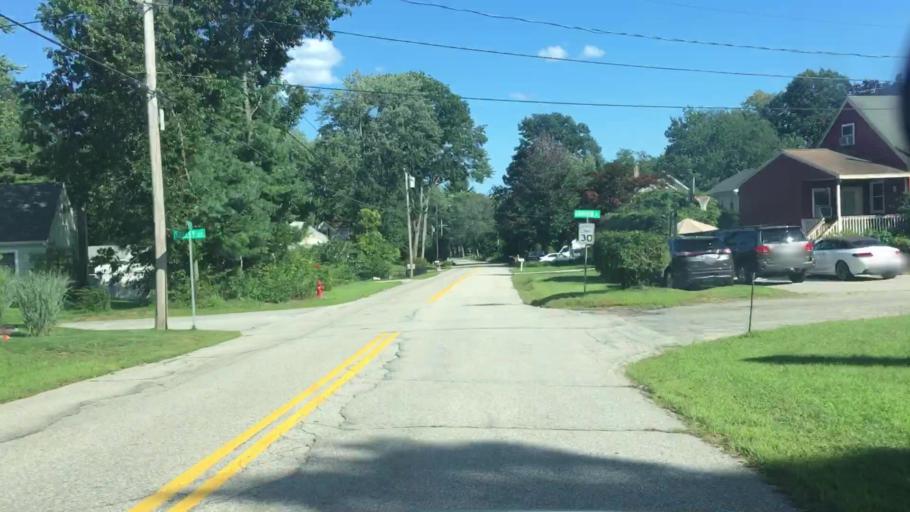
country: US
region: New Hampshire
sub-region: Strafford County
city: Dover
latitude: 43.1594
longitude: -70.8739
